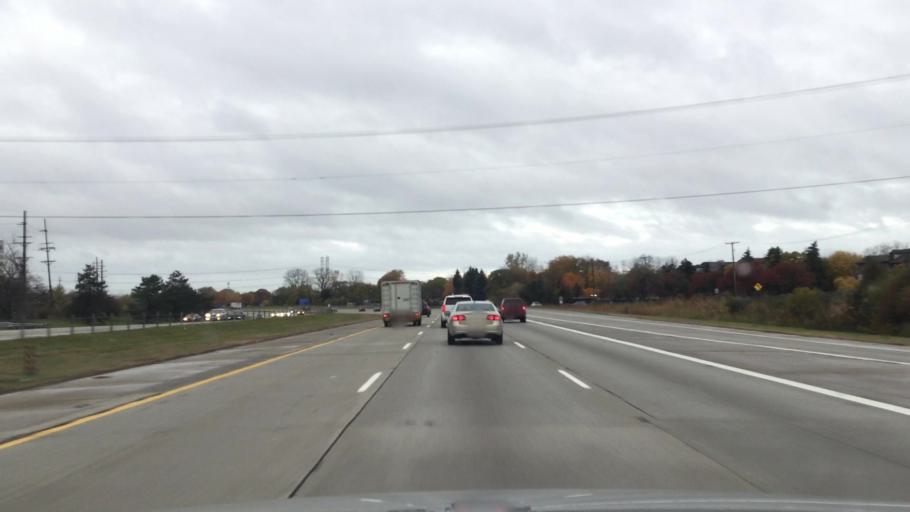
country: US
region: Michigan
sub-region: Wayne County
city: Belleville
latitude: 42.2208
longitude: -83.4442
